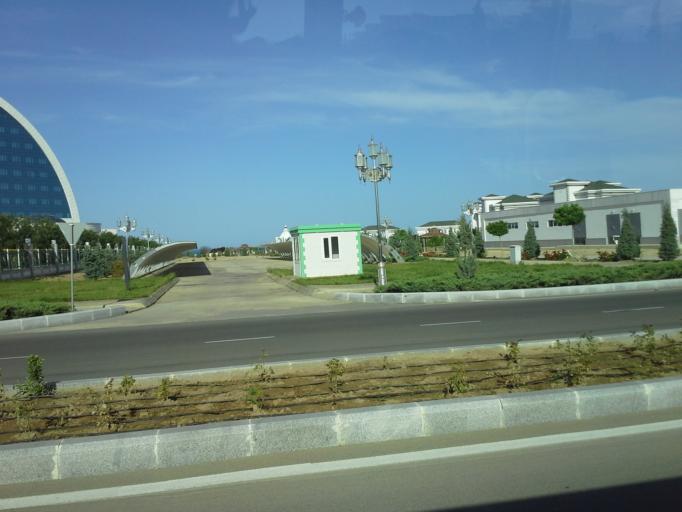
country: TM
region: Balkan
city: Turkmenbasy
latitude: 39.9820
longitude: 52.8265
